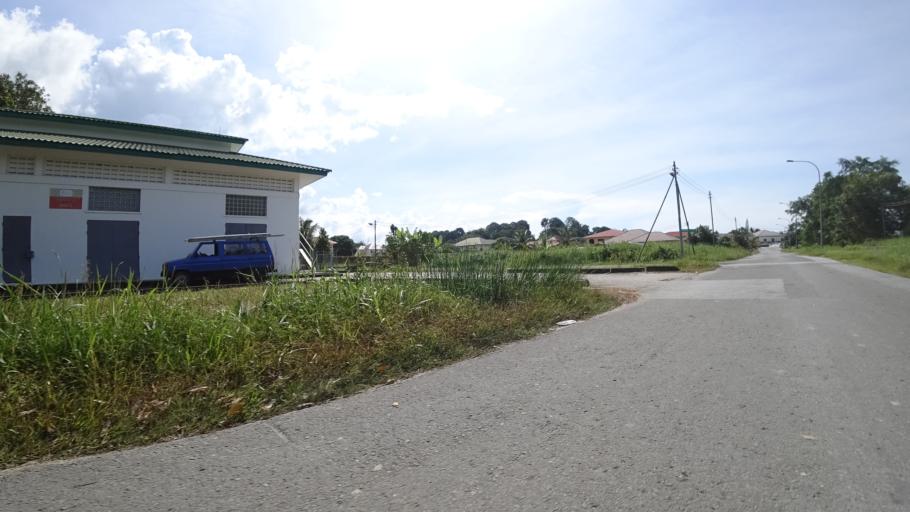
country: BN
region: Brunei and Muara
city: Bandar Seri Begawan
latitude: 4.8729
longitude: 114.8486
